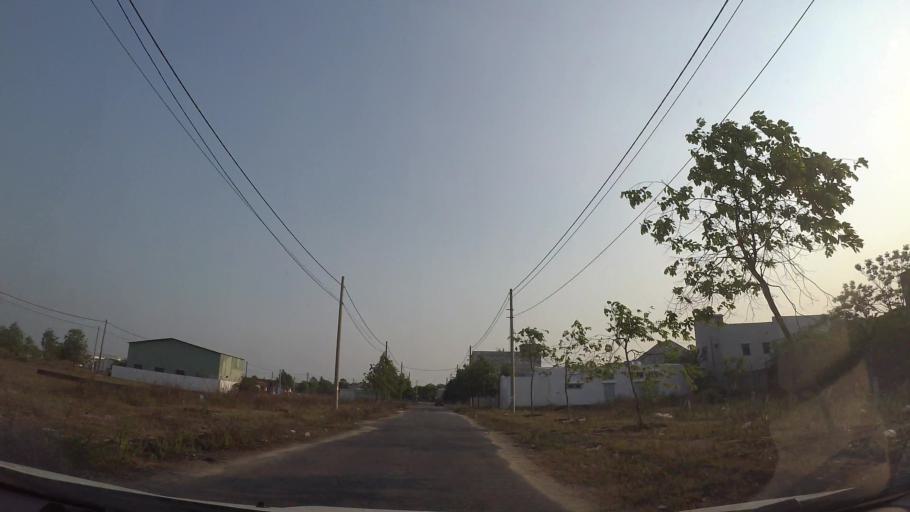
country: VN
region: Da Nang
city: Ngu Hanh Son
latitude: 15.9660
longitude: 108.2555
